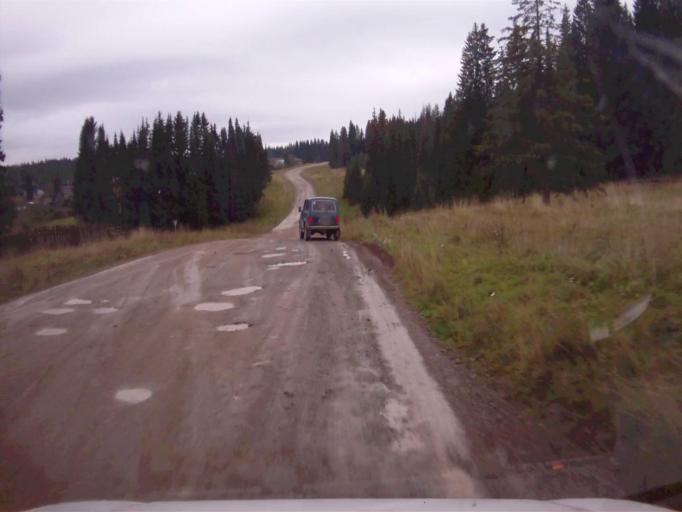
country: RU
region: Chelyabinsk
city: Nyazepetrovsk
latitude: 56.0636
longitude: 59.5668
